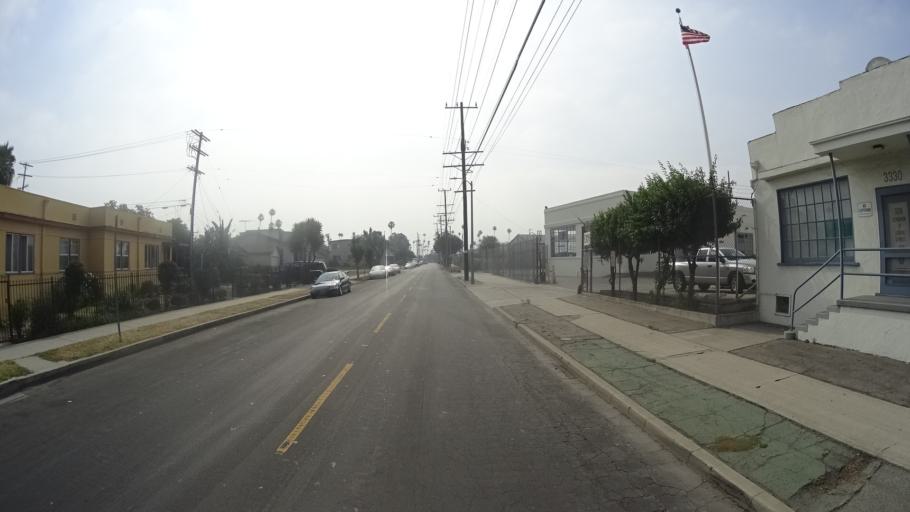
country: US
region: California
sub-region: Los Angeles County
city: View Park-Windsor Hills
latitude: 34.0235
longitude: -118.3327
